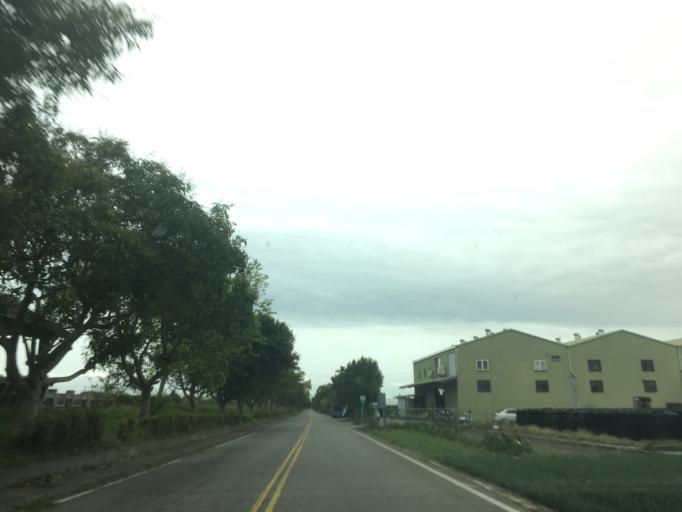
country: TW
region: Taiwan
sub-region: Taitung
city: Taitung
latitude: 22.8025
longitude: 121.1349
